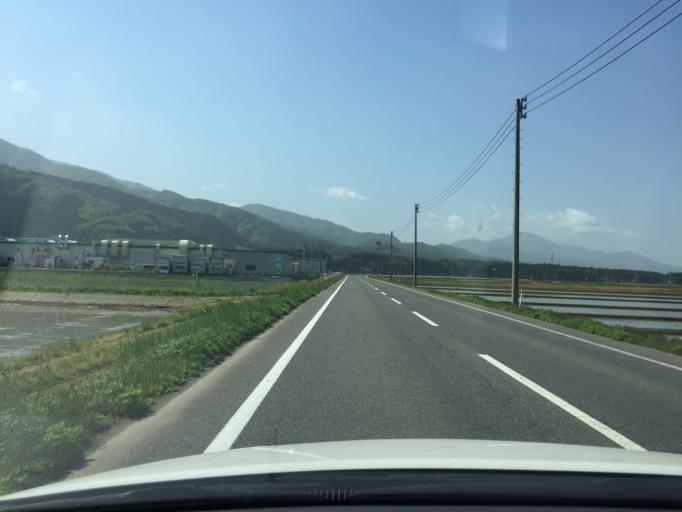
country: JP
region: Niigata
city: Gosen
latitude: 37.7256
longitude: 139.2311
